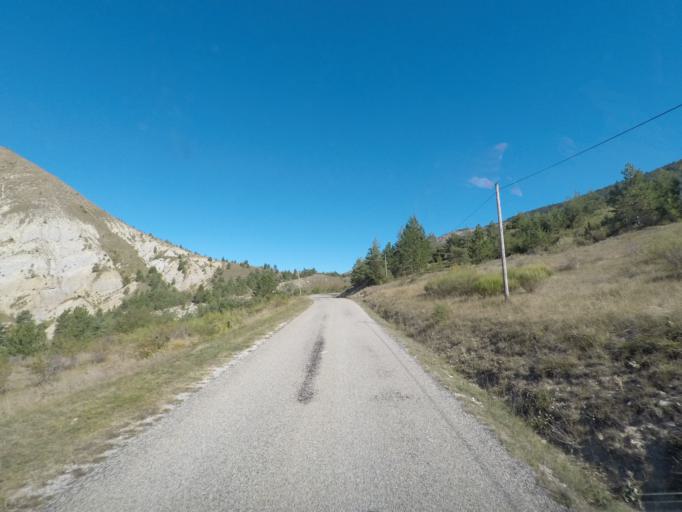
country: FR
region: Rhone-Alpes
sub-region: Departement de la Drome
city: Die
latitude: 44.5359
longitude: 5.3679
